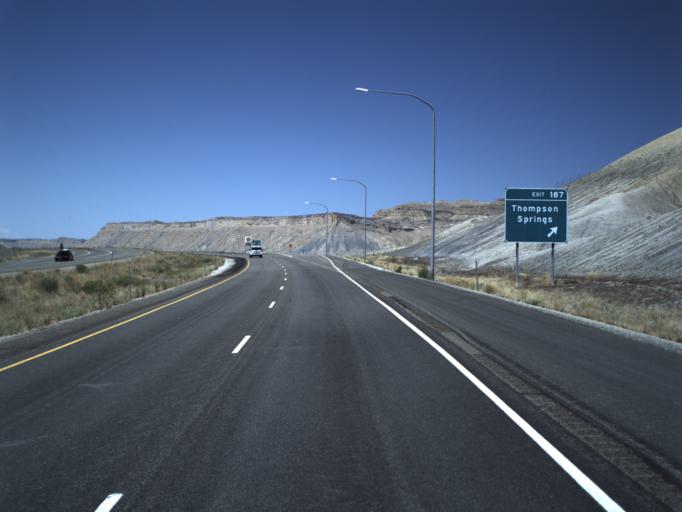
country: US
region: Utah
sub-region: Grand County
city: Moab
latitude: 38.9612
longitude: -109.7151
